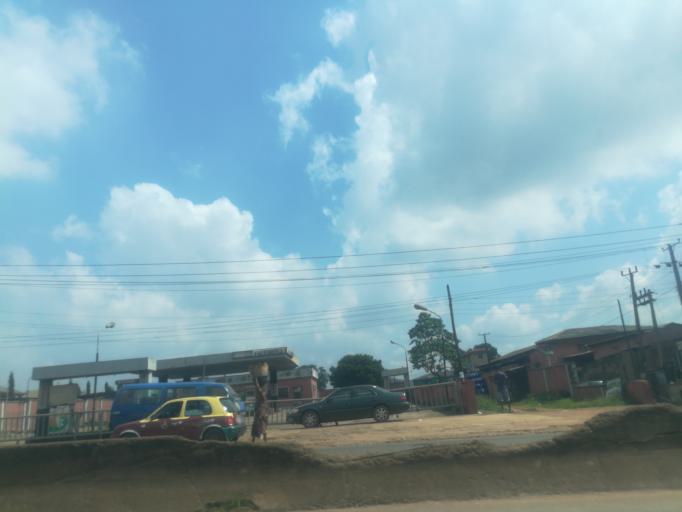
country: NG
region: Oyo
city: Ibadan
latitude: 7.3962
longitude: 3.9523
